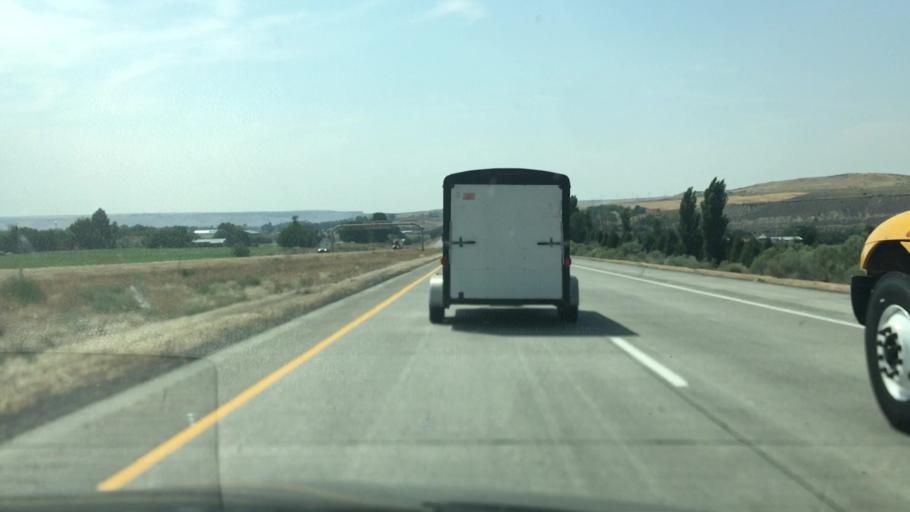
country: US
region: Idaho
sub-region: Elmore County
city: Glenns Ferry
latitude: 42.9617
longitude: -115.2647
